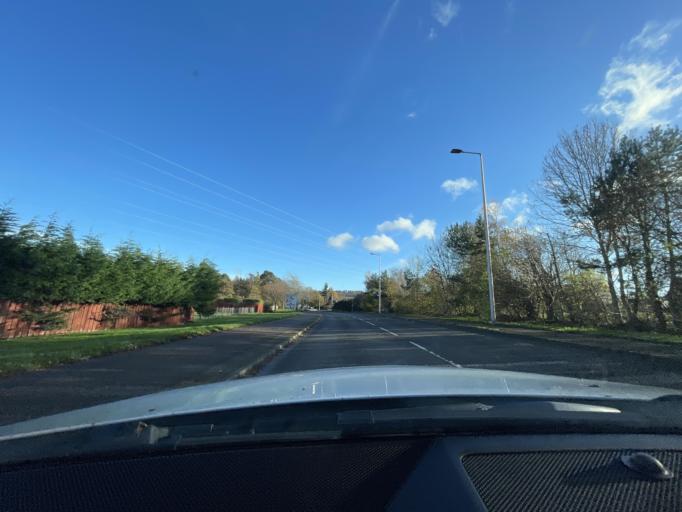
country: GB
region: Scotland
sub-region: Highland
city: Inverness
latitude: 57.4483
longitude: -4.2413
